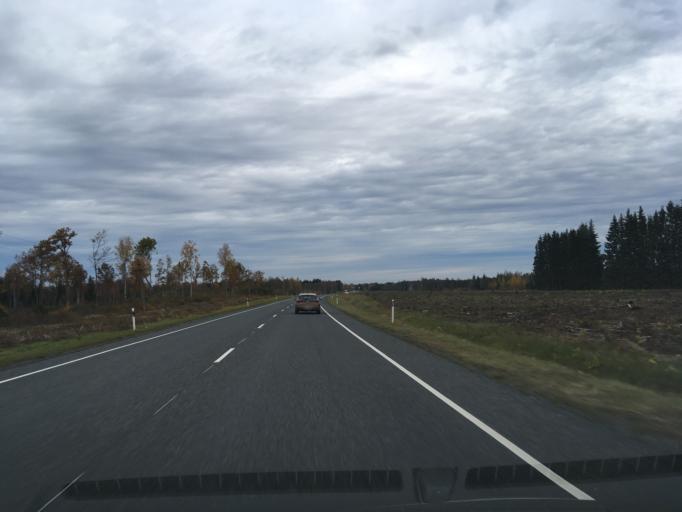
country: EE
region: Harju
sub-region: Nissi vald
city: Turba
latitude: 58.9806
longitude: 24.0577
